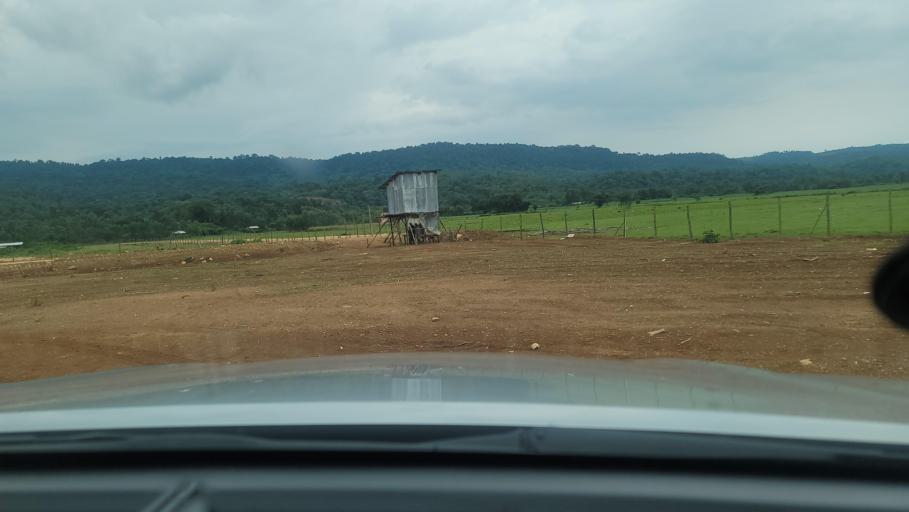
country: ET
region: Oromiya
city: Agaro
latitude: 7.7628
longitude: 36.3159
